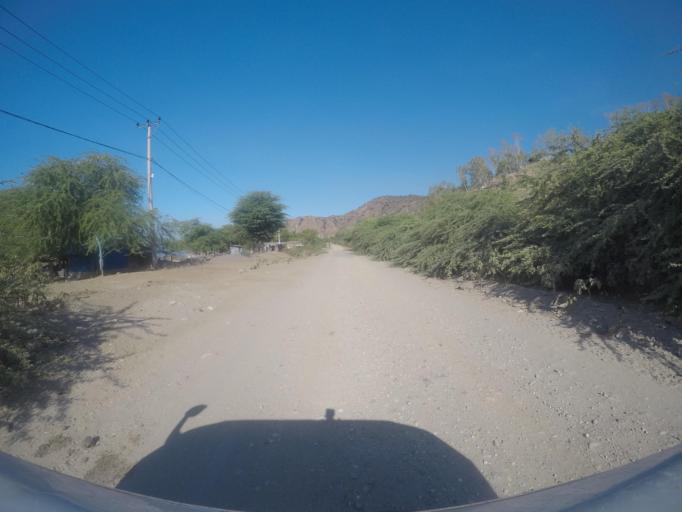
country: TL
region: Dili
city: Dili
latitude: -8.5279
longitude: 125.6325
